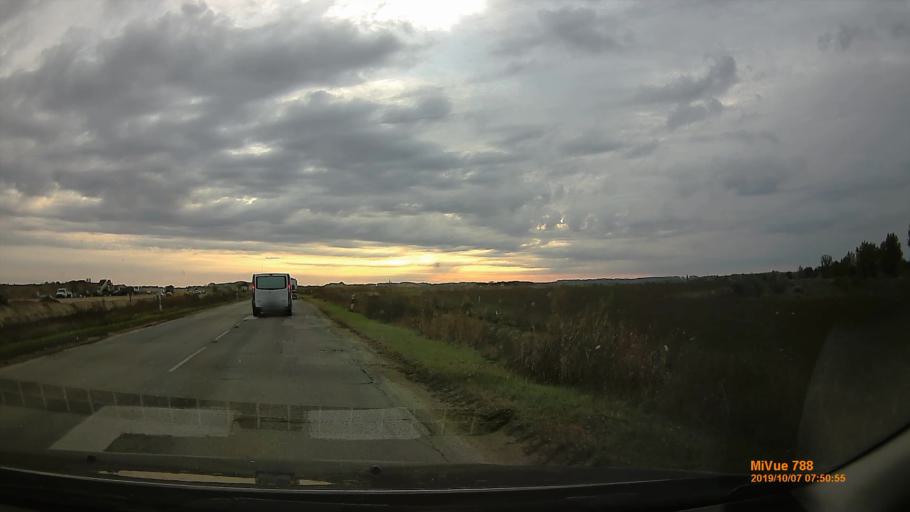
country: HU
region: Bacs-Kiskun
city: Tiszakecske
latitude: 46.8693
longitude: 20.0922
